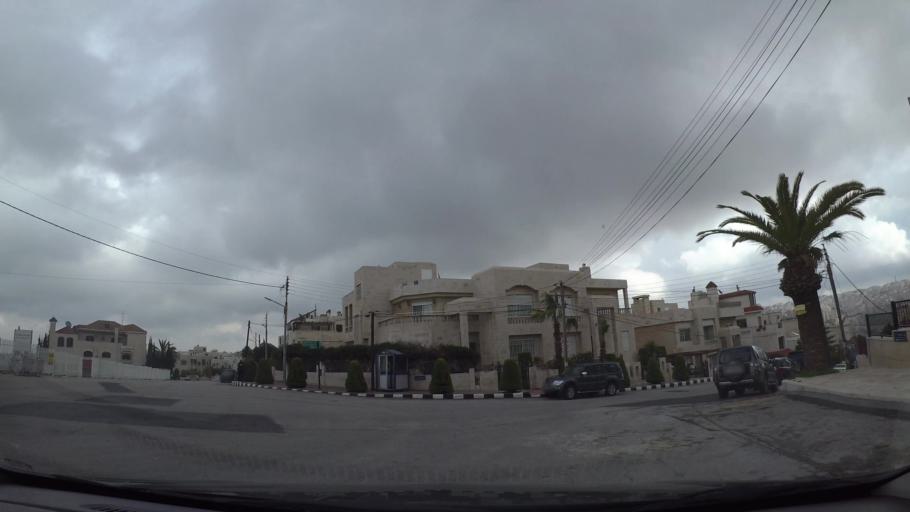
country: JO
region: Amman
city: Amman
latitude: 31.9436
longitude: 35.8997
